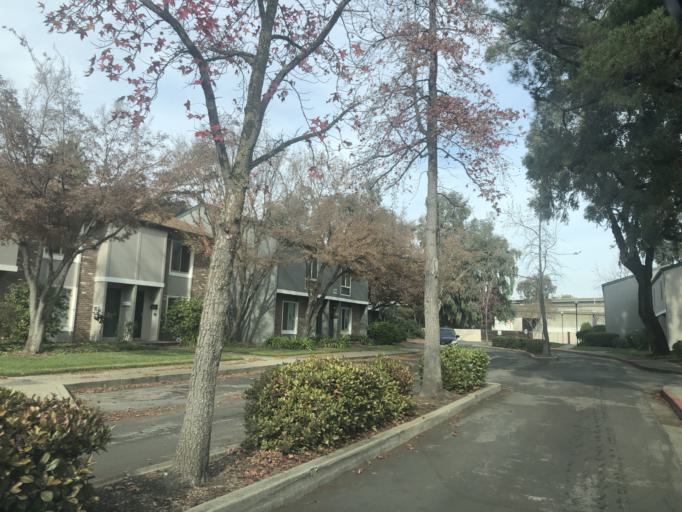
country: US
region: California
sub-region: Contra Costa County
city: Concord
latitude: 38.0031
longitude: -122.0393
